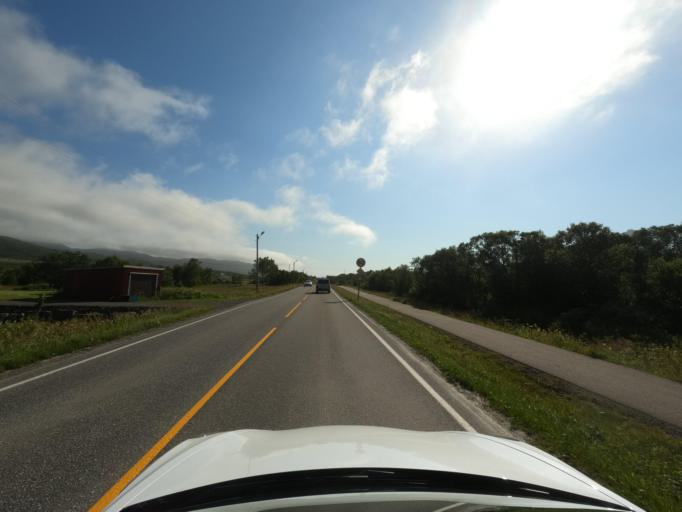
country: NO
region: Nordland
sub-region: Vestvagoy
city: Evjen
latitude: 68.2344
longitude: 13.7432
